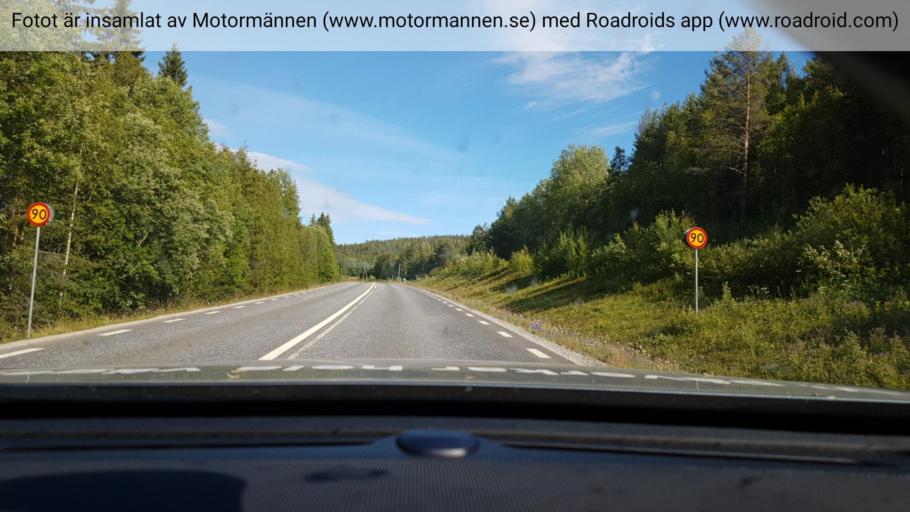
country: SE
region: Vaesterbotten
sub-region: Lycksele Kommun
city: Soderfors
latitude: 64.7049
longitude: 18.3240
